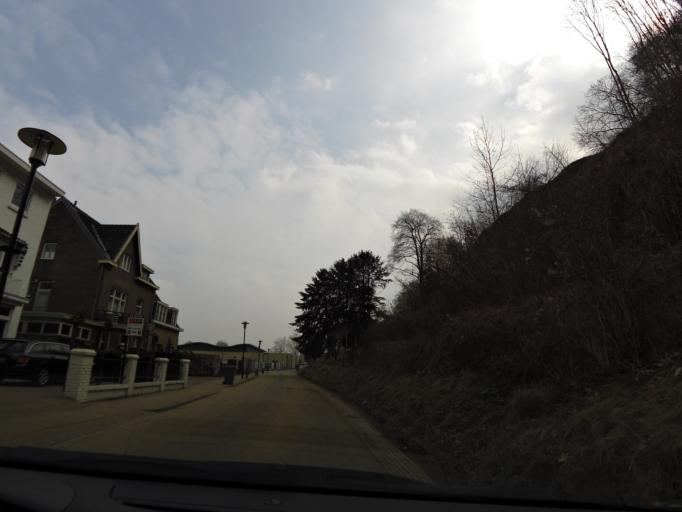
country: NL
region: Limburg
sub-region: Valkenburg aan de Geul
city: Broekhem
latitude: 50.8653
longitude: 5.8247
